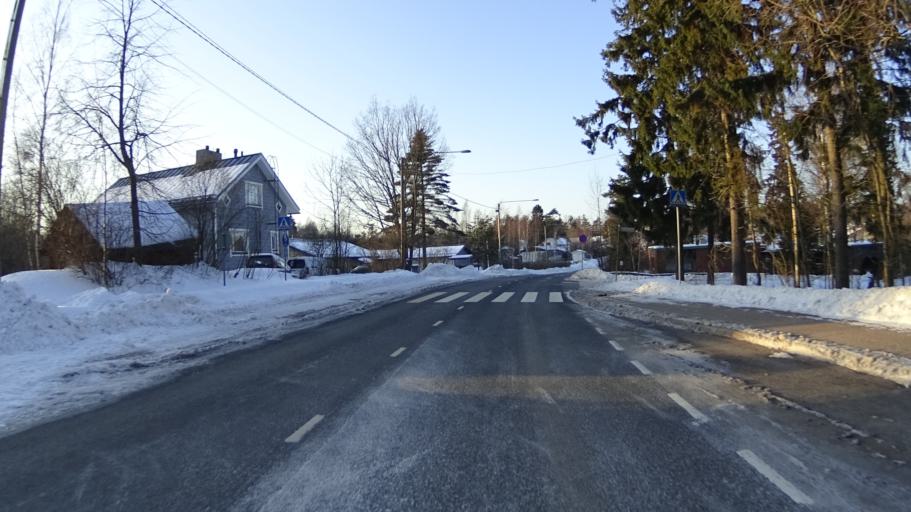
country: FI
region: Uusimaa
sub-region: Helsinki
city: Vantaa
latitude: 60.2603
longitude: 25.0978
